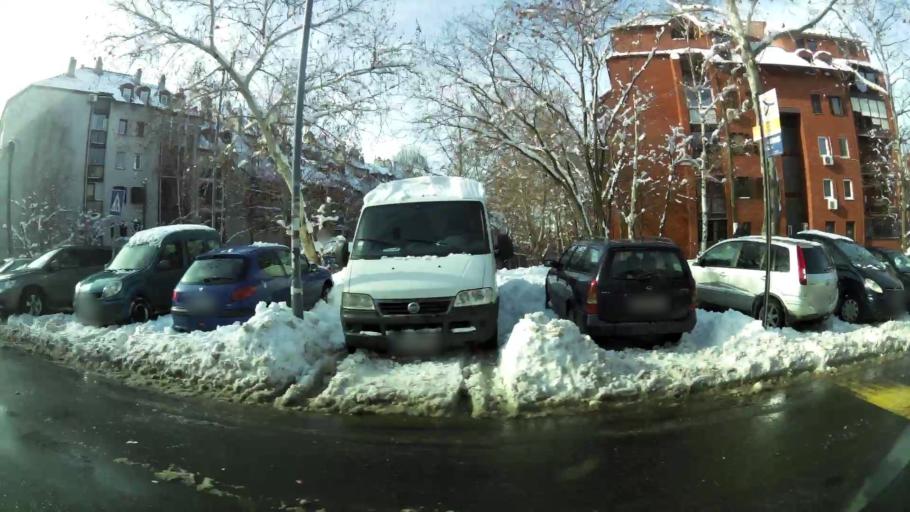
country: RS
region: Central Serbia
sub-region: Belgrade
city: Zvezdara
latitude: 44.7876
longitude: 20.5464
